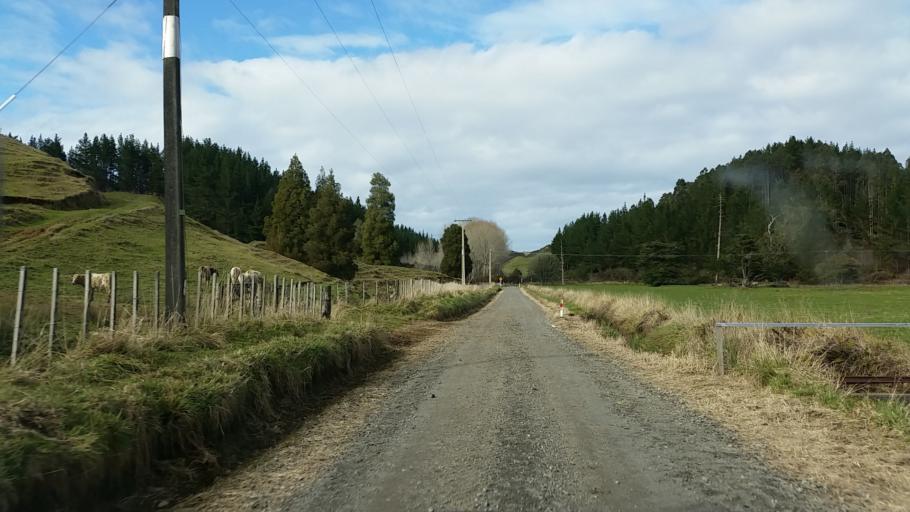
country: NZ
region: Taranaki
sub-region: South Taranaki District
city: Eltham
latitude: -39.2312
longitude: 174.5664
